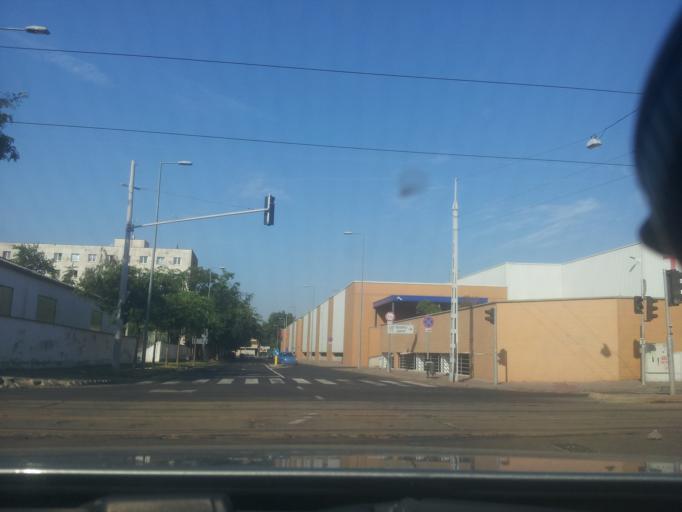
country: HU
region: Budapest
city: Budapest IX. keruelet
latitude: 47.4661
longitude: 19.0815
